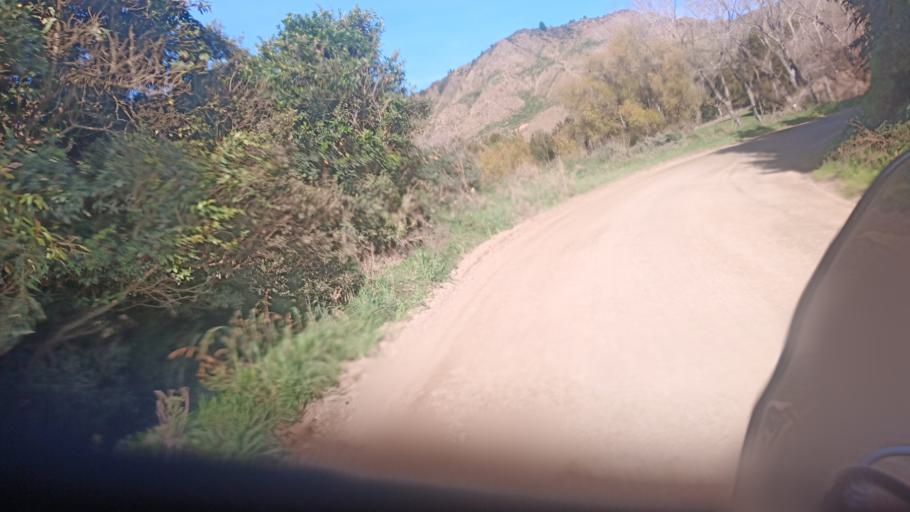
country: NZ
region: Gisborne
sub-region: Gisborne District
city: Gisborne
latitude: -38.4304
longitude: 177.5608
